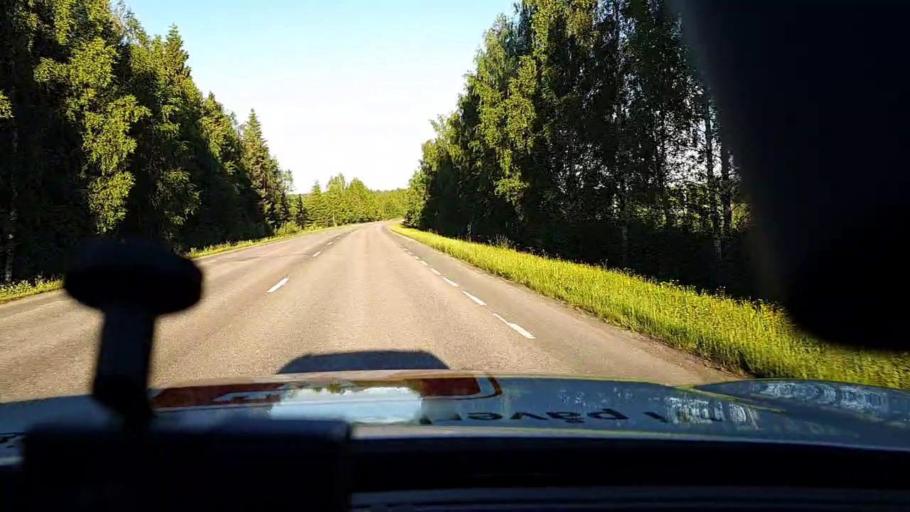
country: SE
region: Norrbotten
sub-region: Lulea Kommun
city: Lulea
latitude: 65.6136
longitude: 22.1564
